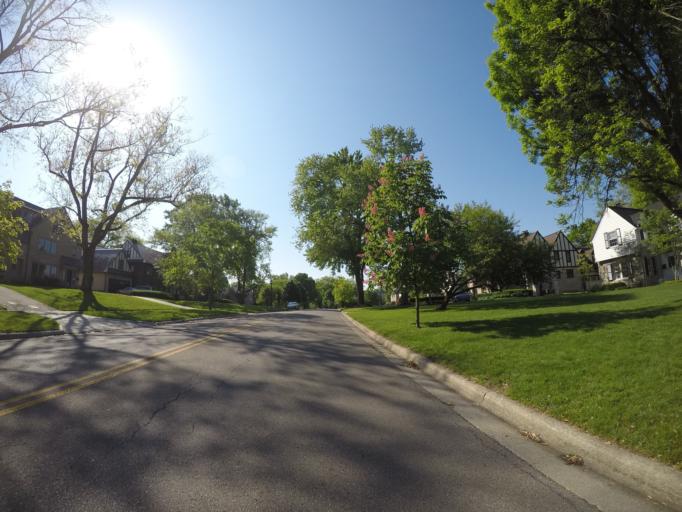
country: US
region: Ohio
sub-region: Franklin County
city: Upper Arlington
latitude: 39.9969
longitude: -83.0650
